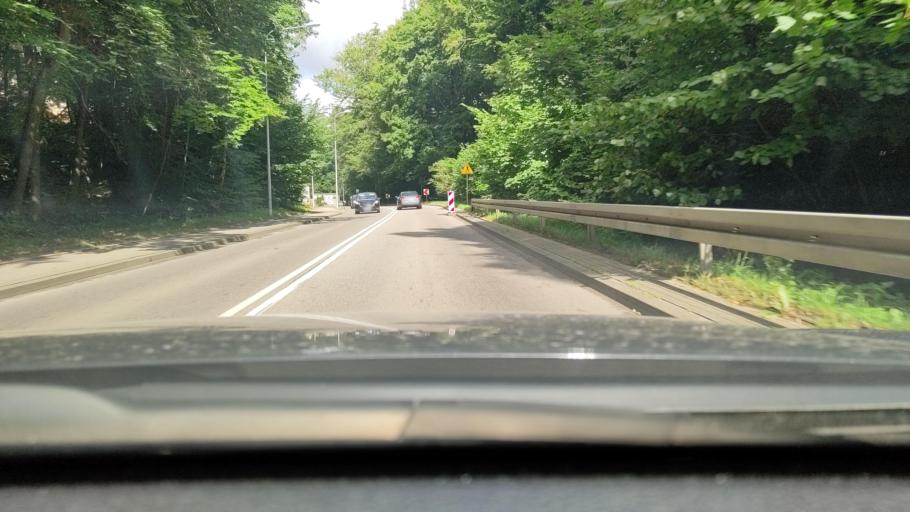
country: PL
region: Pomeranian Voivodeship
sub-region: Powiat wejherowski
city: Wejherowo
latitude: 54.5943
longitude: 18.2350
